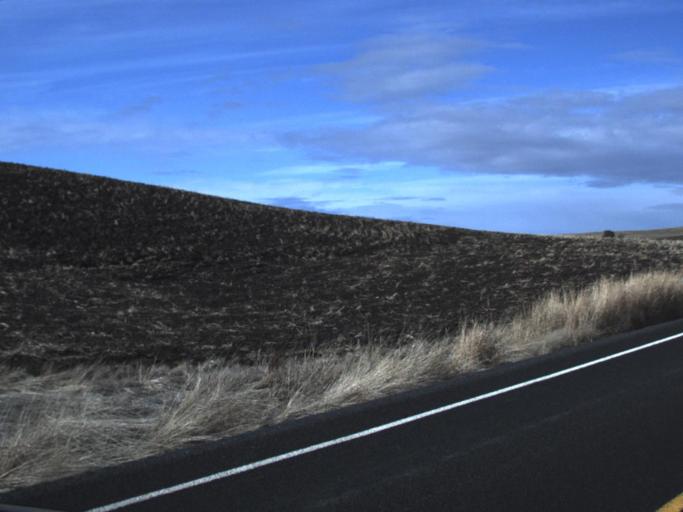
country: US
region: Washington
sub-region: Whitman County
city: Pullman
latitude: 46.9250
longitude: -117.1081
